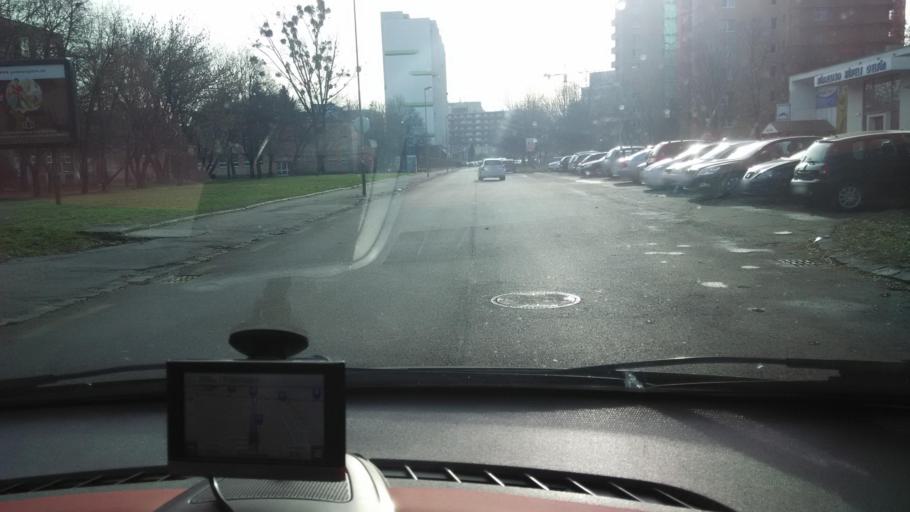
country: SK
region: Bratislavsky
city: Bratislava
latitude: 48.1505
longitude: 17.1426
